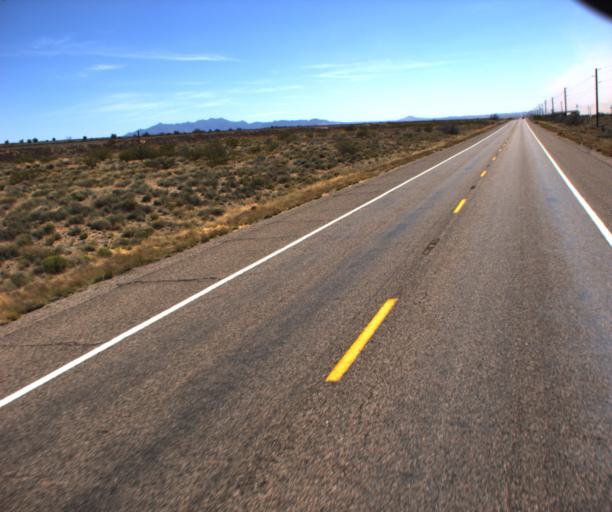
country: US
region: Arizona
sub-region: Mohave County
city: New Kingman-Butler
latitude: 35.4019
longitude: -113.8339
